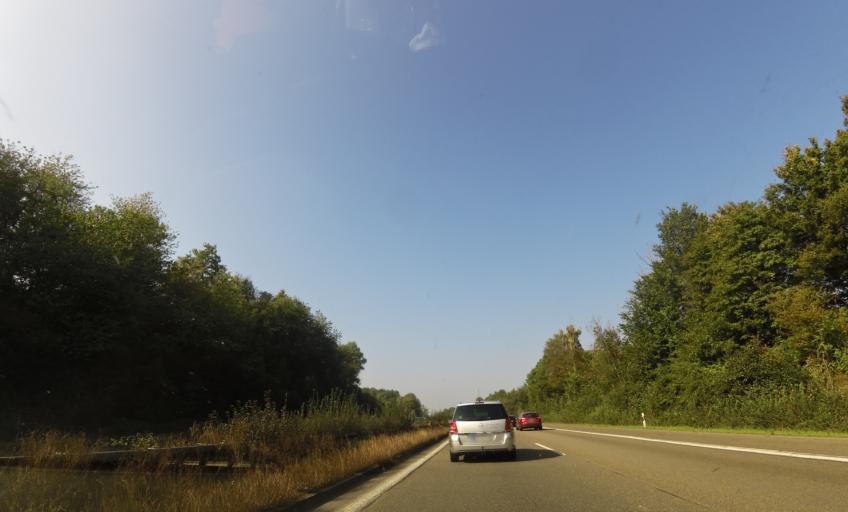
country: DE
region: Baden-Wuerttemberg
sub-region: Karlsruhe Region
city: Zuzenhausen
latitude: 49.2566
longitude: 8.8349
